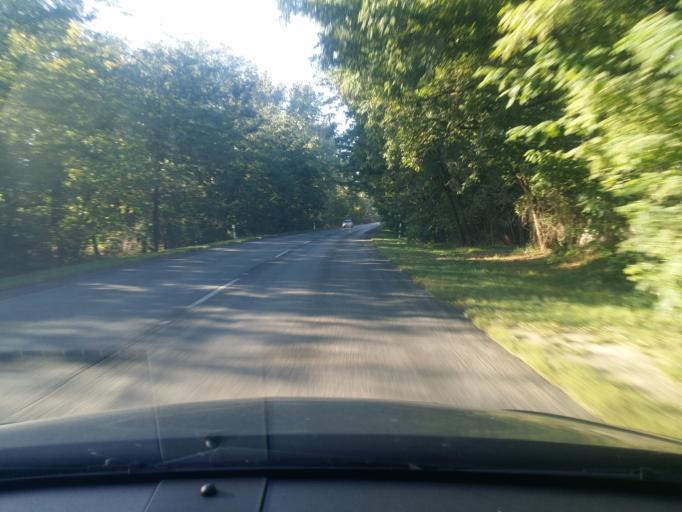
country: HU
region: Csongrad
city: Szatymaz
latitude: 46.3374
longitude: 20.0660
